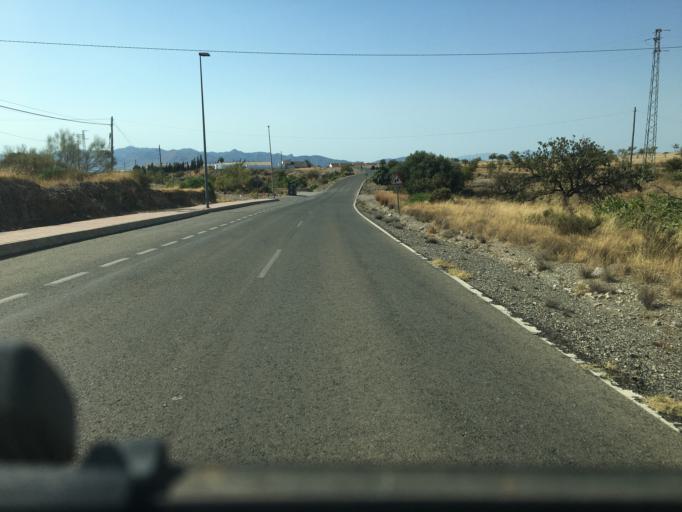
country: ES
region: Andalusia
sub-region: Provincia de Almeria
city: Huercal-Overa
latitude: 37.4458
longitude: -1.9822
